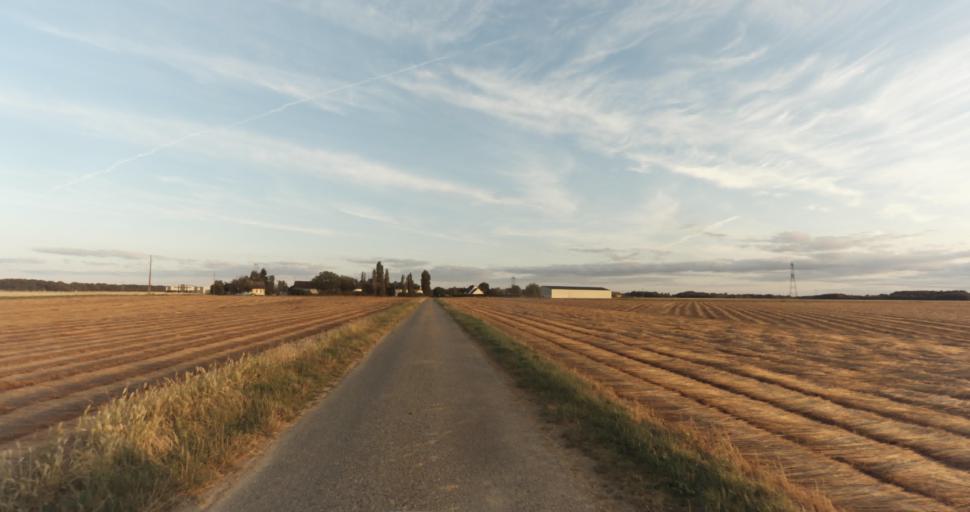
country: FR
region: Haute-Normandie
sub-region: Departement de l'Eure
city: La Madeleine-de-Nonancourt
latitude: 48.8560
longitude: 1.2126
